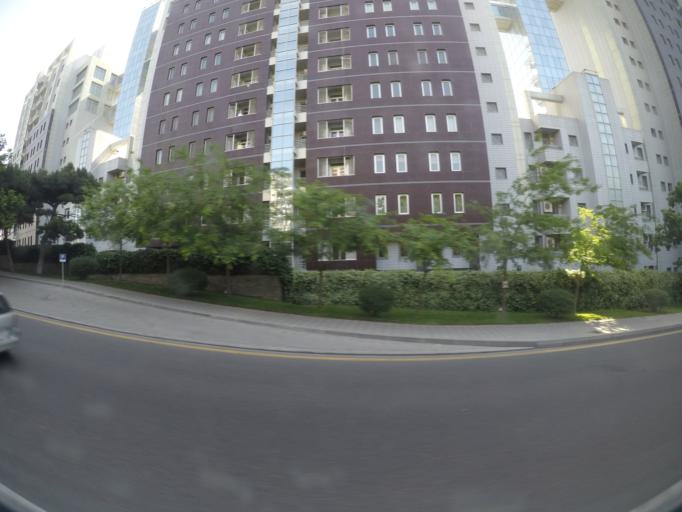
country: AZ
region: Baki
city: Badamdar
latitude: 40.3666
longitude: 49.8248
